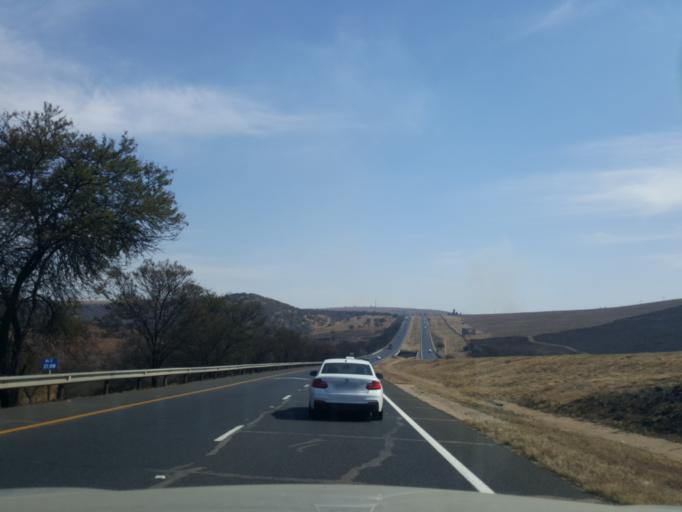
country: ZA
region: Mpumalanga
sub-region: Nkangala District Municipality
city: Witbank
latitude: -25.8791
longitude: 29.3080
